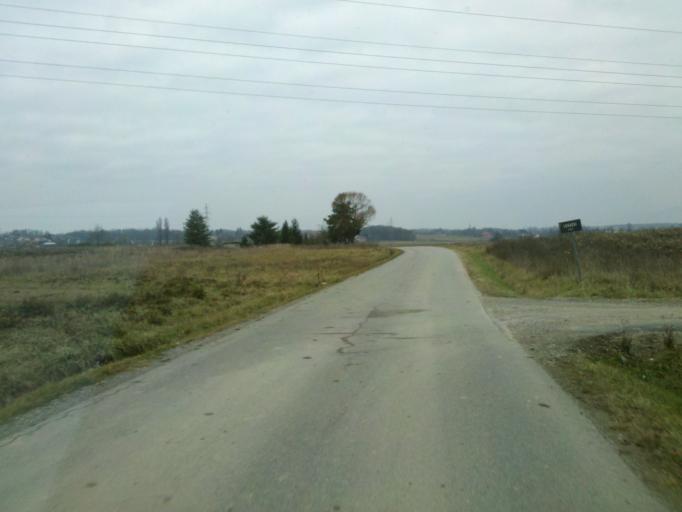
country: HR
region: Grad Zagreb
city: Strmec
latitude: 45.6848
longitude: 15.8700
